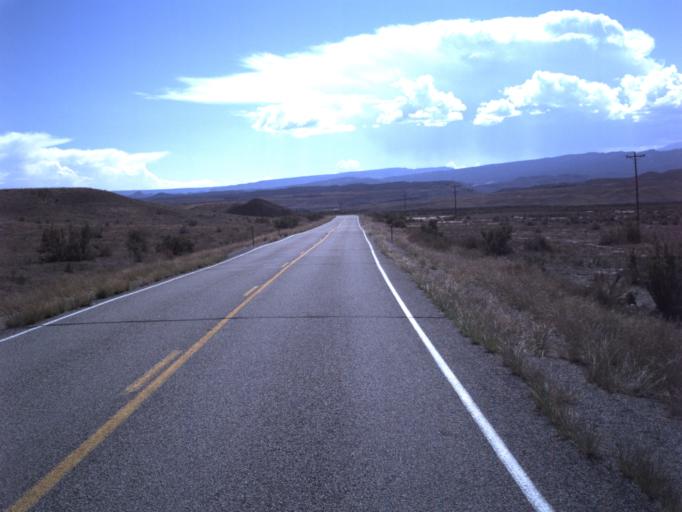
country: US
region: Utah
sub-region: Grand County
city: Moab
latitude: 38.8743
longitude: -109.3050
